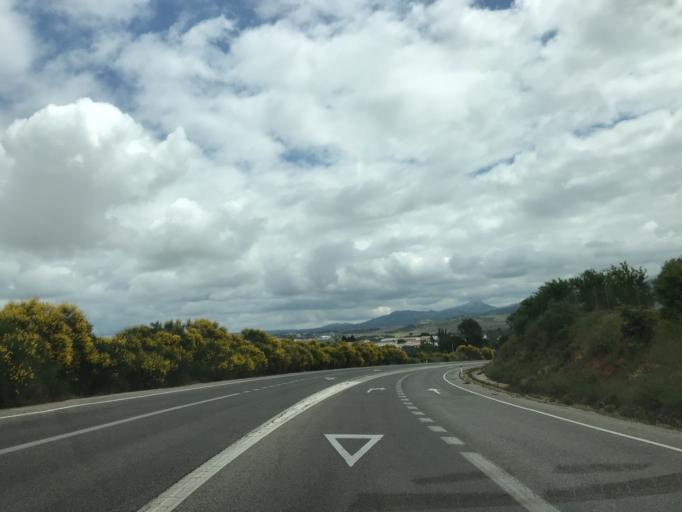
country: ES
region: Andalusia
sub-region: Provincia de Malaga
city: Ronda
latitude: 36.7240
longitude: -5.1707
